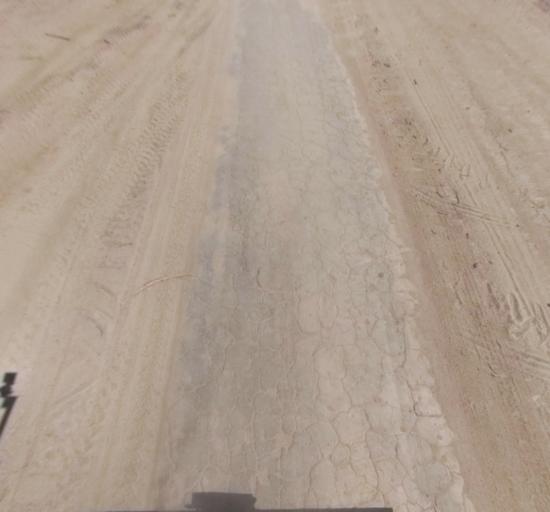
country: US
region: California
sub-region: Madera County
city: Madera
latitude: 36.9441
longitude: -120.1467
